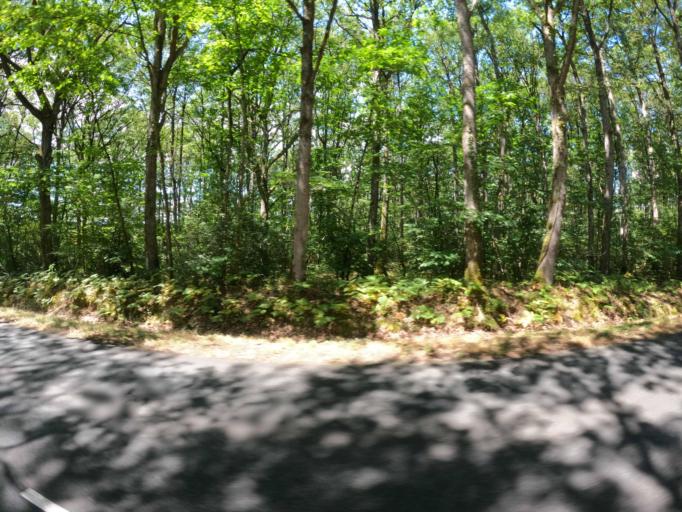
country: FR
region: Pays de la Loire
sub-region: Departement de Maine-et-Loire
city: Champigne
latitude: 47.6210
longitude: -0.5832
